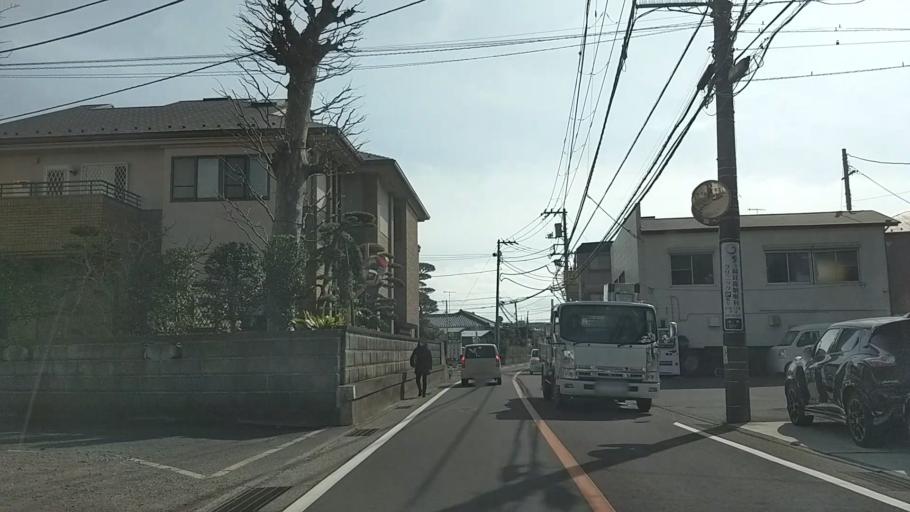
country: JP
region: Kanagawa
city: Chigasaki
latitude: 35.3398
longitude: 139.3828
